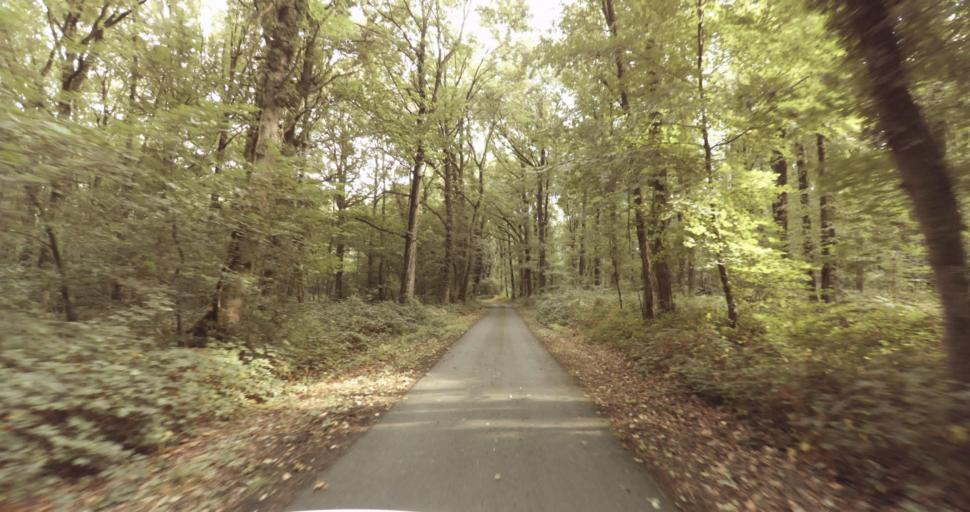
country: FR
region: Lower Normandy
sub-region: Departement de l'Orne
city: Vimoutiers
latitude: 48.9233
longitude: 0.1485
